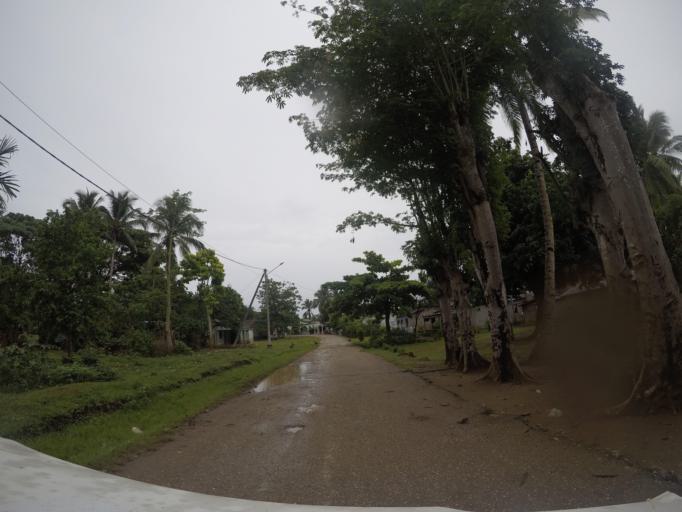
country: TL
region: Lautem
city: Lospalos
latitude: -8.5236
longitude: 126.9999
